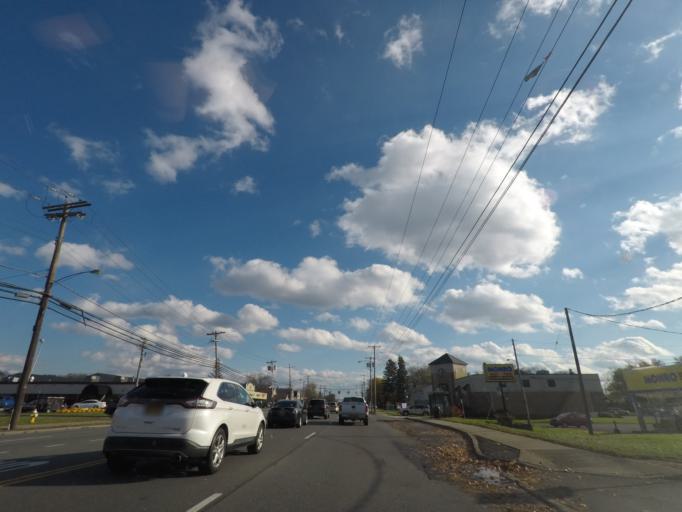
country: US
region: New York
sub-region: Albany County
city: Colonie
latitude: 42.7152
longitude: -73.8302
